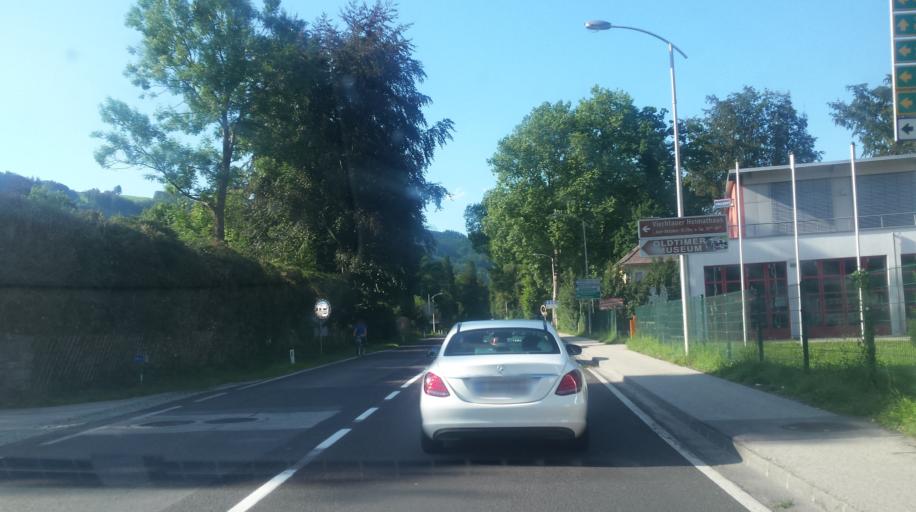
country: AT
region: Upper Austria
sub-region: Politischer Bezirk Gmunden
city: Altmunster
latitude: 47.8945
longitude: 13.7659
